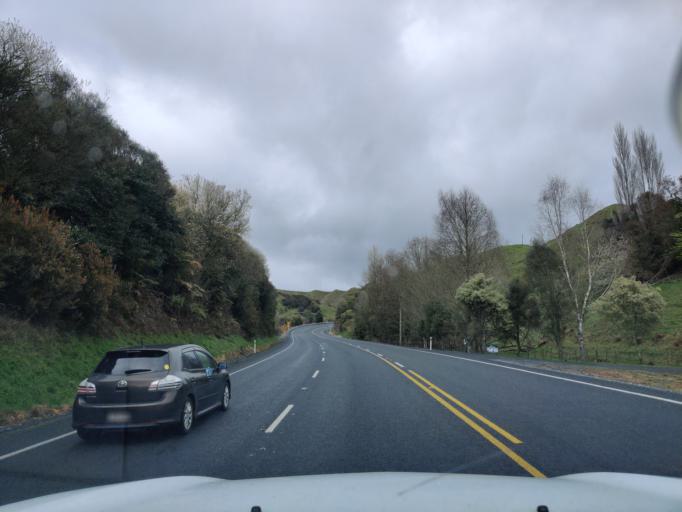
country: NZ
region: Waikato
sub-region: Otorohanga District
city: Otorohanga
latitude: -38.6320
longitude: 175.2094
